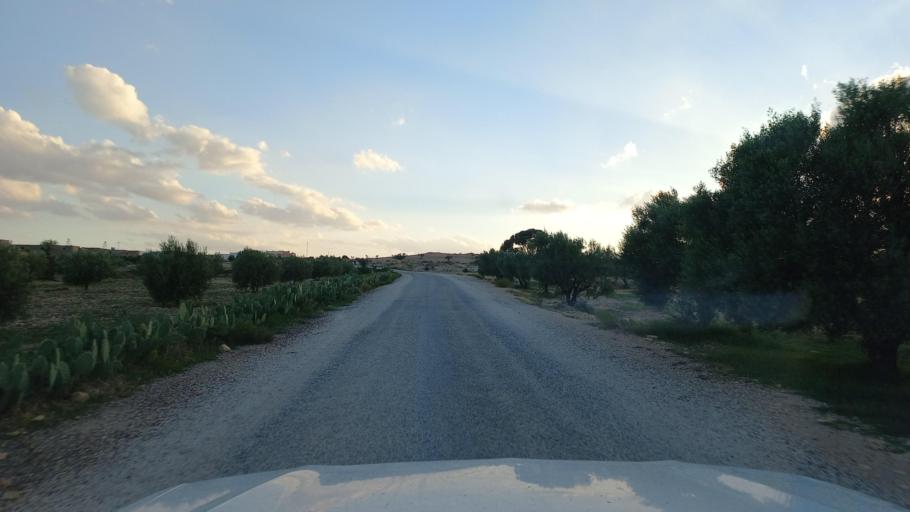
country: TN
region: Al Qasrayn
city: Sbiba
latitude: 35.3755
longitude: 9.0631
